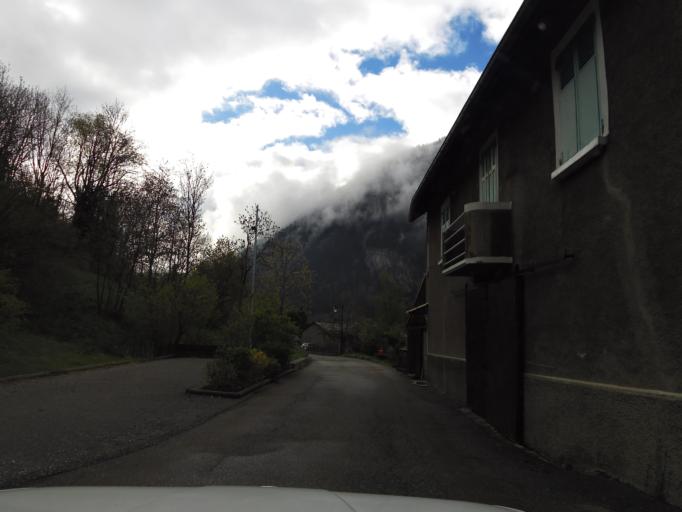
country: FR
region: Rhone-Alpes
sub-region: Departement de la Savoie
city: Saint-Michel-de-Maurienne
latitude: 45.2104
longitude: 6.5538
